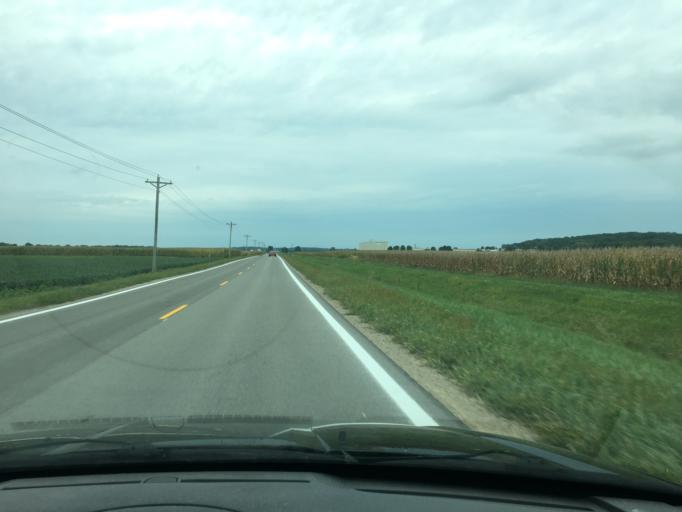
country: US
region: Ohio
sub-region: Champaign County
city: Urbana
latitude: 40.1781
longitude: -83.7826
